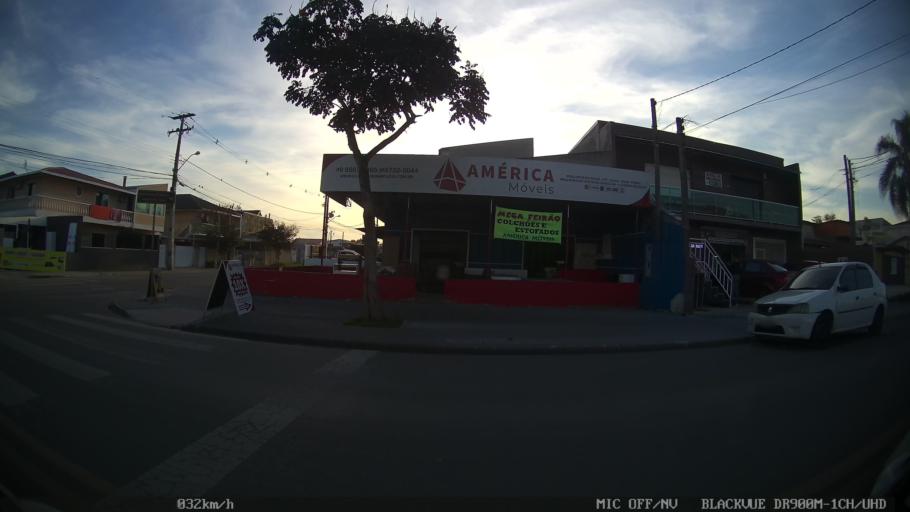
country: BR
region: Parana
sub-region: Pinhais
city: Pinhais
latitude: -25.4447
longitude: -49.1626
